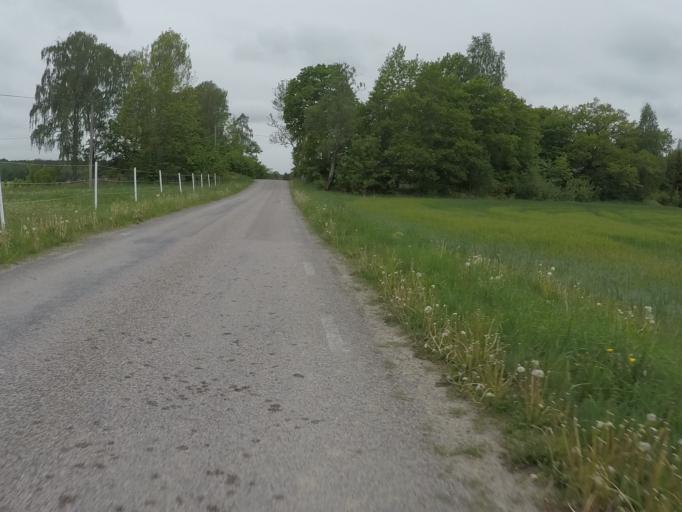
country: SE
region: Vaestmanland
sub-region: Hallstahammars Kommun
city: Kolback
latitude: 59.5478
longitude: 16.3007
